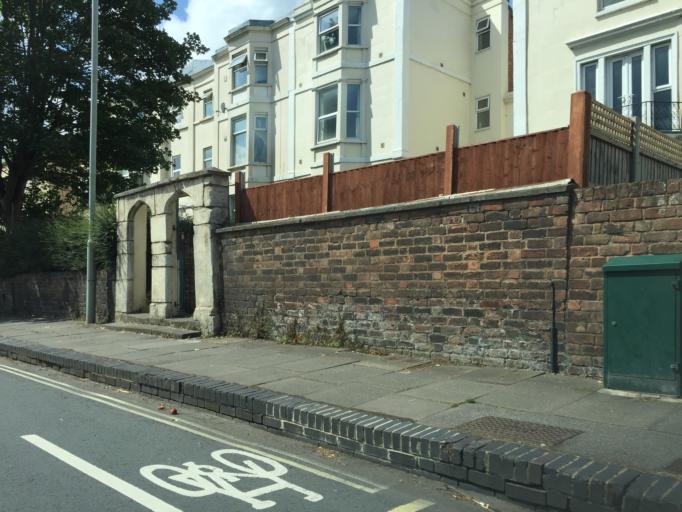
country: GB
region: England
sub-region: Gloucestershire
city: Gloucester
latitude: 51.8738
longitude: -2.2411
